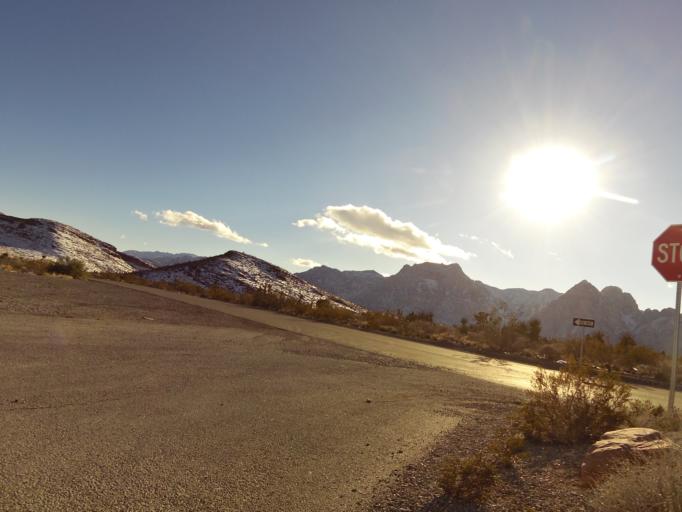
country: US
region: Nevada
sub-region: Clark County
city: Summerlin South
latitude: 36.1319
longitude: -115.4241
